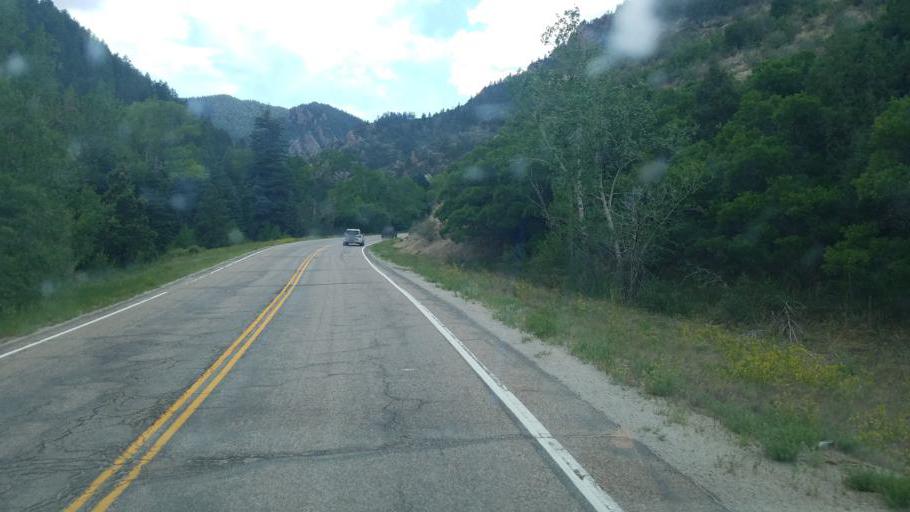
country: US
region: Colorado
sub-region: Fremont County
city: Florence
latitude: 38.1749
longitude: -105.1474
